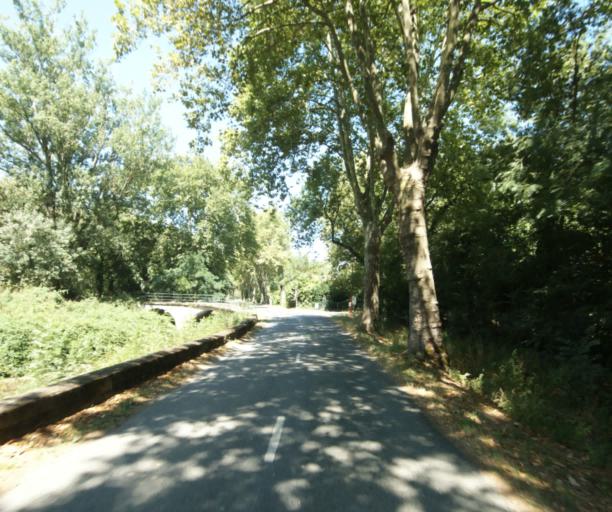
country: FR
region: Midi-Pyrenees
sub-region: Departement de la Haute-Garonne
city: Revel
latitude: 43.4957
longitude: 1.9677
